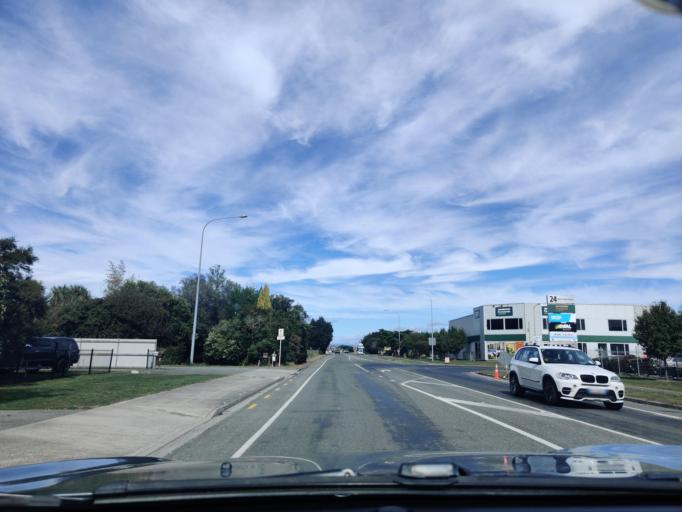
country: NZ
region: Tasman
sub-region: Tasman District
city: Richmond
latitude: -41.3466
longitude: 173.1660
